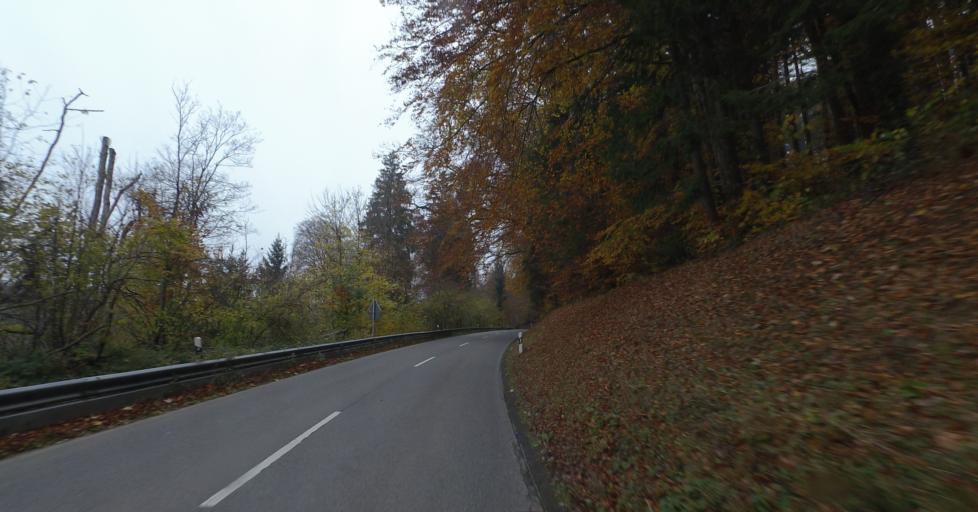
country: DE
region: Bavaria
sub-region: Upper Bavaria
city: Seeon-Seebruck
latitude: 47.9616
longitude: 12.5095
